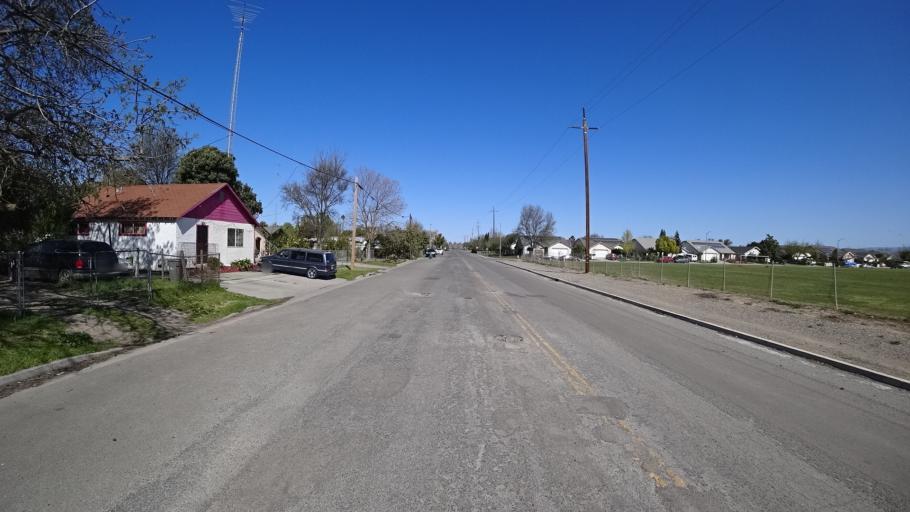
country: US
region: California
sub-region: Glenn County
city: Hamilton City
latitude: 39.7431
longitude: -122.0072
